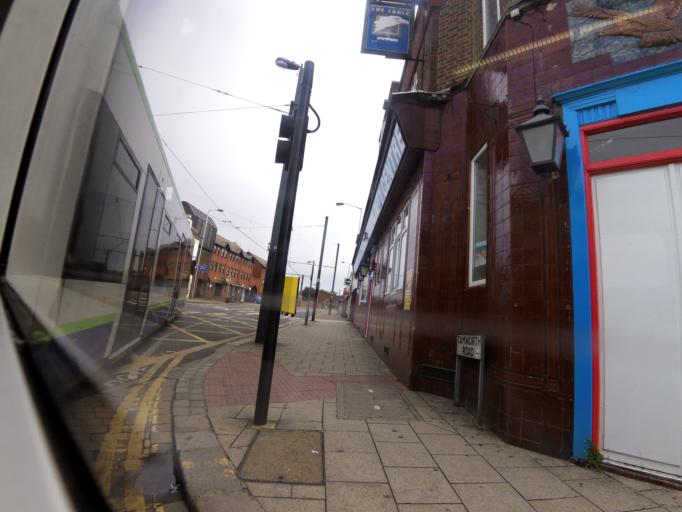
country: GB
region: England
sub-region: Greater London
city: Croydon
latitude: 51.3742
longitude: -0.1053
